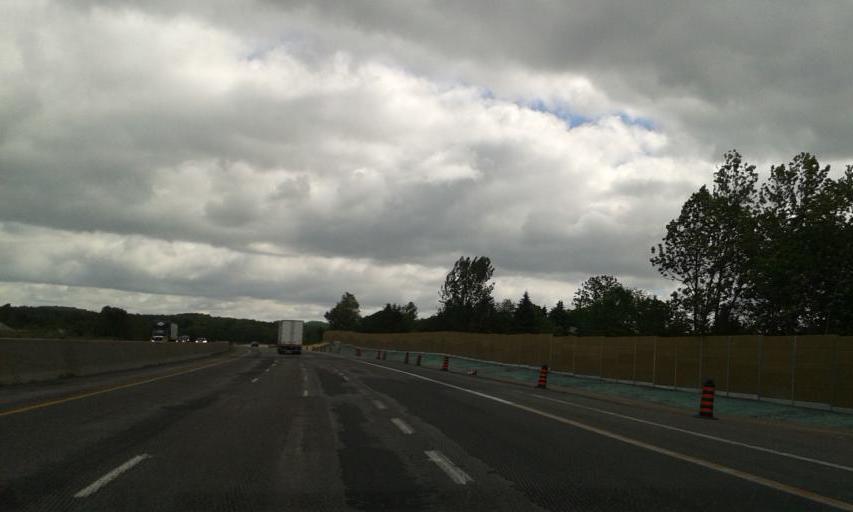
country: CA
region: Ontario
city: Cobourg
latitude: 43.9876
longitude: -78.1691
